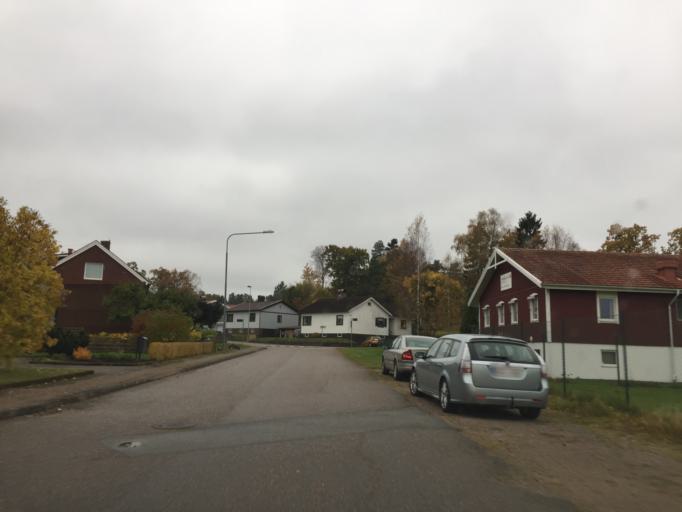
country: SE
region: Vaestra Goetaland
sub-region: Trollhattan
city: Trollhattan
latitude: 58.2887
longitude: 12.2706
